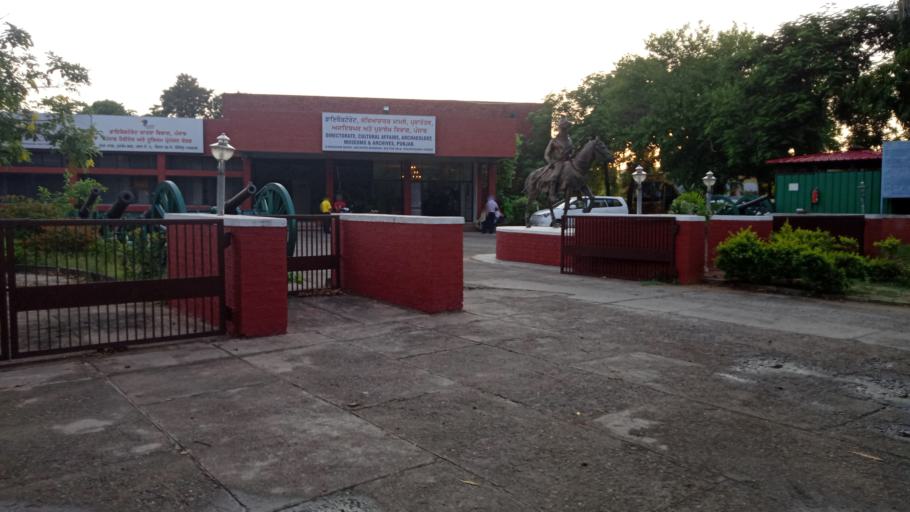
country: IN
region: Chandigarh
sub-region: Chandigarh
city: Chandigarh
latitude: 30.7486
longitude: 76.7508
